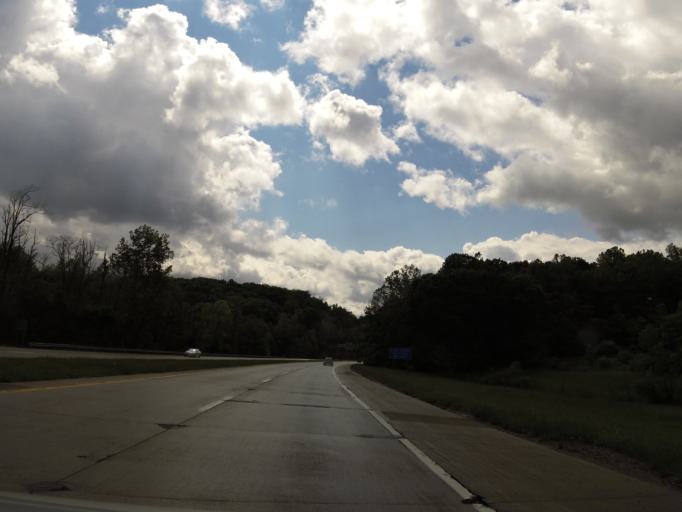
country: US
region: Ohio
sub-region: Athens County
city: Athens
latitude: 39.3504
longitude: -82.0865
